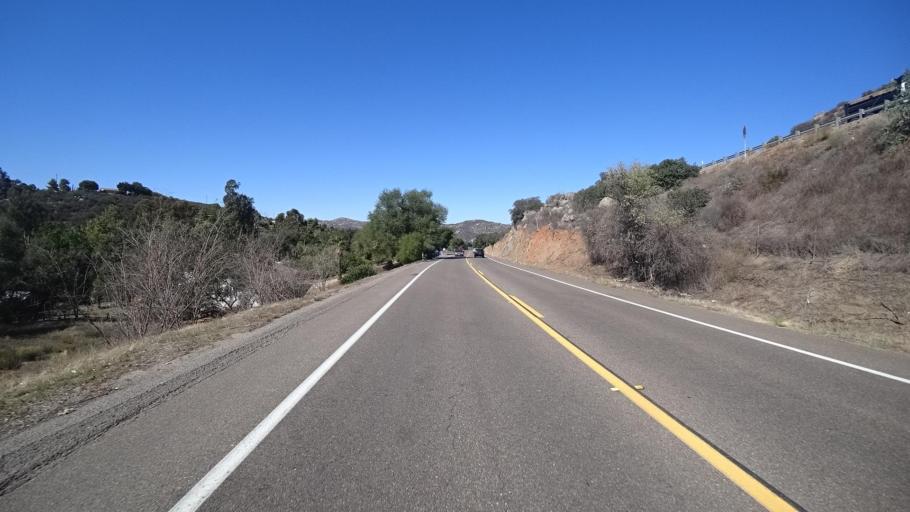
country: US
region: California
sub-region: San Diego County
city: Alpine
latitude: 32.8392
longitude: -116.7879
